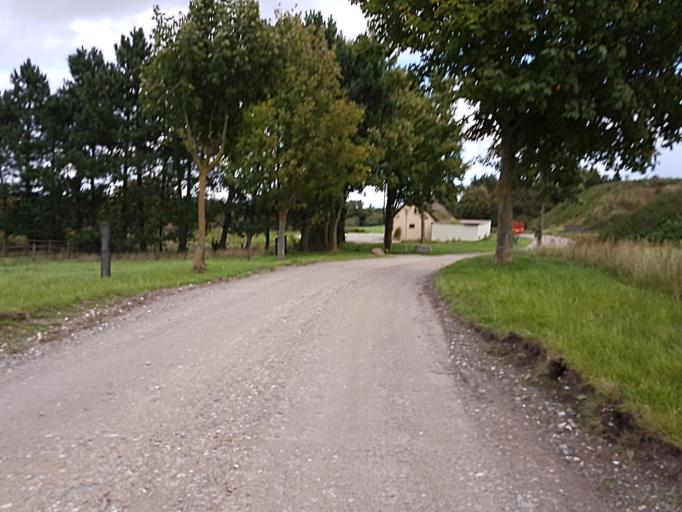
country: DK
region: Zealand
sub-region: Roskilde Kommune
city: Jyllinge
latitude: 55.7489
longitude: 12.1286
